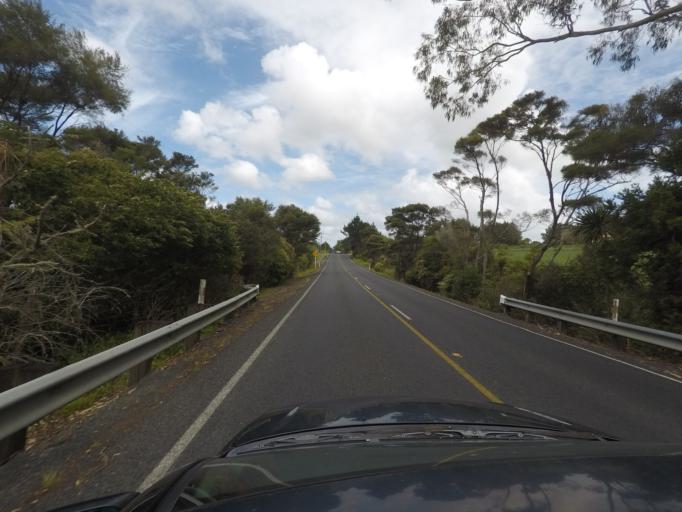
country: NZ
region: Auckland
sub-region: Auckland
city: Parakai
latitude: -36.6413
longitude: 174.5101
